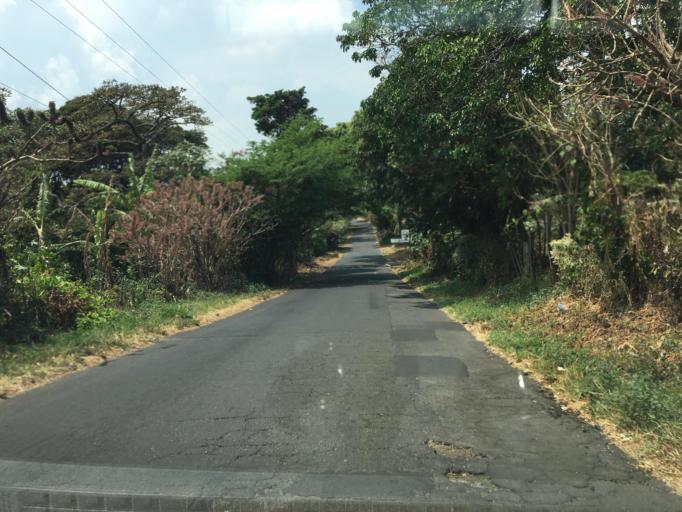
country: GT
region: Escuintla
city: San Vicente Pacaya
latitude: 14.3756
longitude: -90.5564
